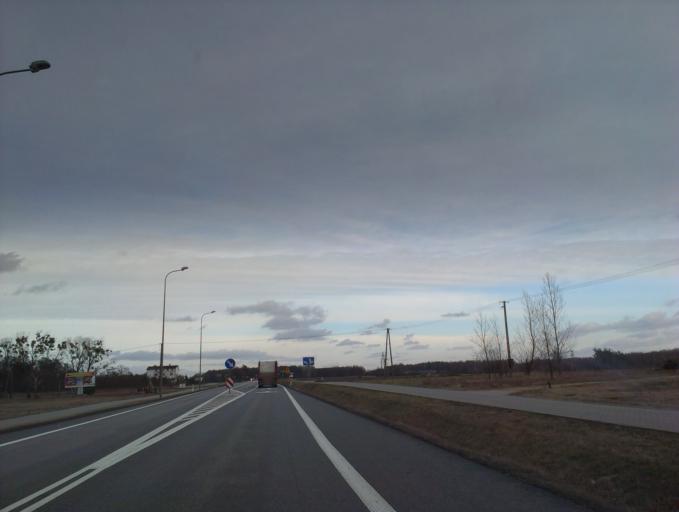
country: PL
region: Kujawsko-Pomorskie
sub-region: Powiat lipnowski
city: Skepe
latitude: 52.8927
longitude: 19.4304
